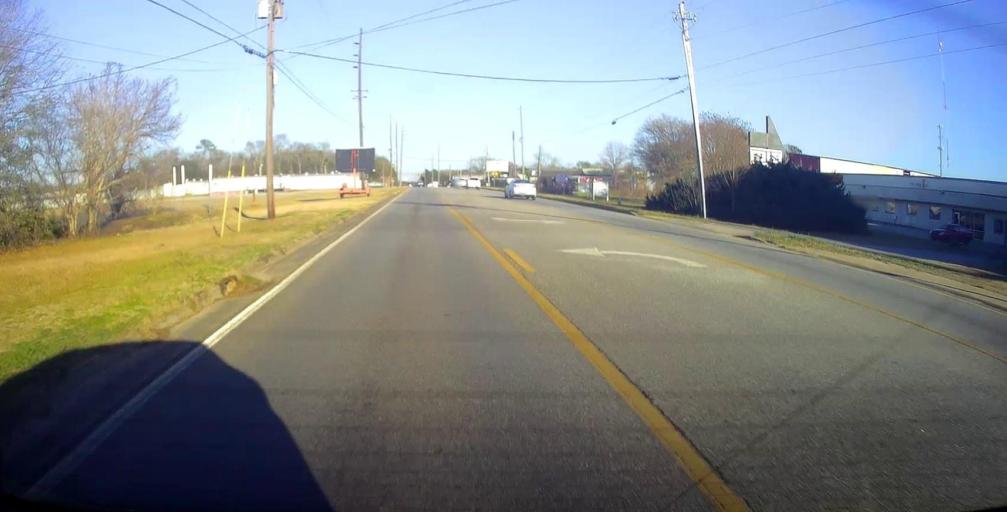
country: US
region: Georgia
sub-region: Dougherty County
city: Albany
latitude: 31.6227
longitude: -84.1911
